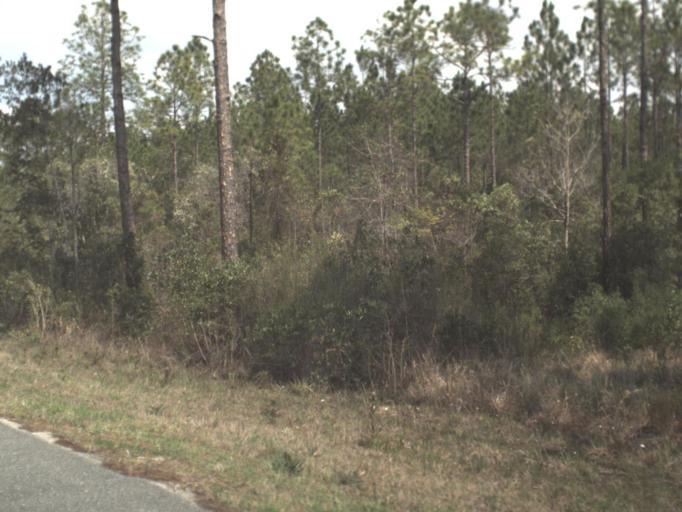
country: US
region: Florida
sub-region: Franklin County
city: Apalachicola
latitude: 29.9326
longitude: -84.9769
